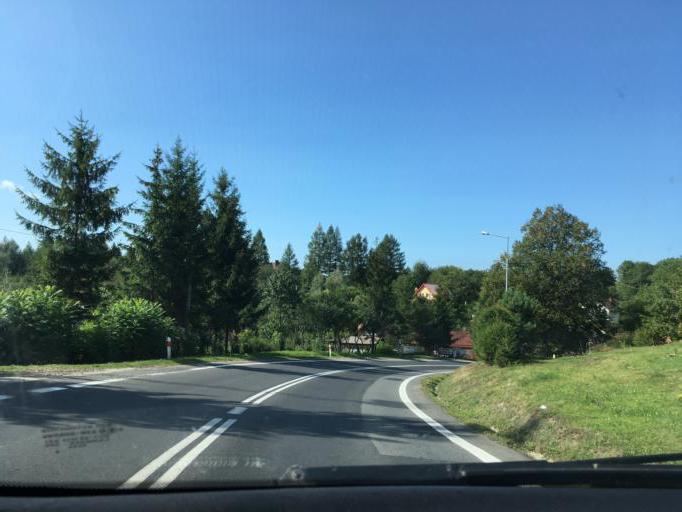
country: PL
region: Subcarpathian Voivodeship
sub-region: Powiat leski
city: Lesko
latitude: 49.4643
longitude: 22.3413
